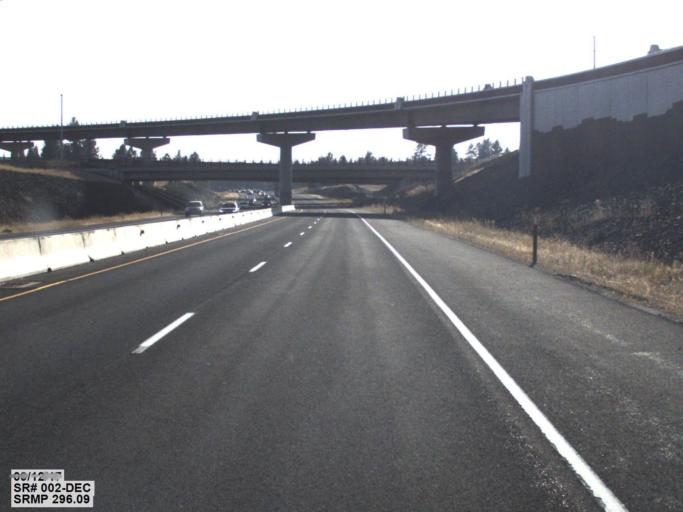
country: US
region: Washington
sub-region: Spokane County
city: Mead
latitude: 47.7767
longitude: -117.3704
